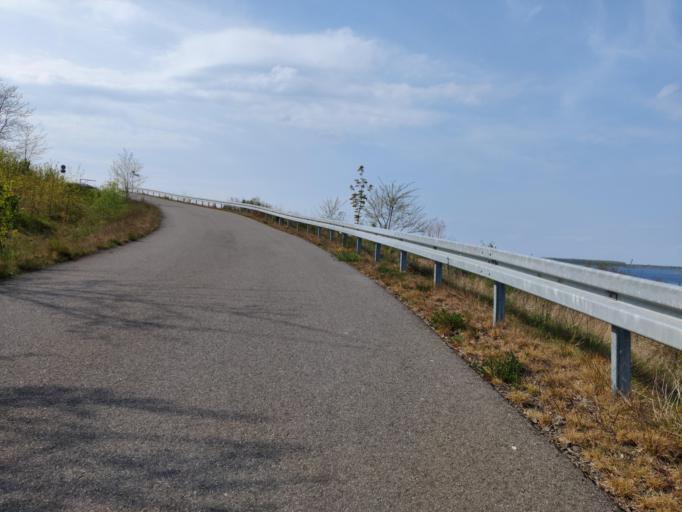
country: DE
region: Saxony
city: Zwenkau
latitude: 51.2175
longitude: 12.3463
